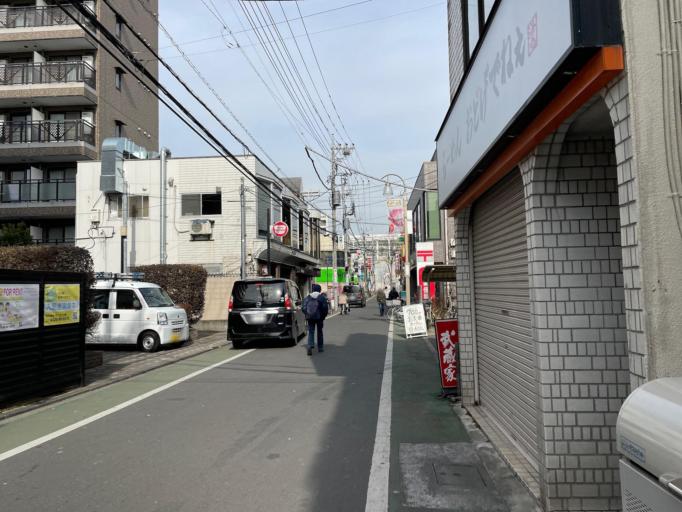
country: JP
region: Tokyo
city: Nishi-Tokyo-shi
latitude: 35.7002
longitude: 139.5244
